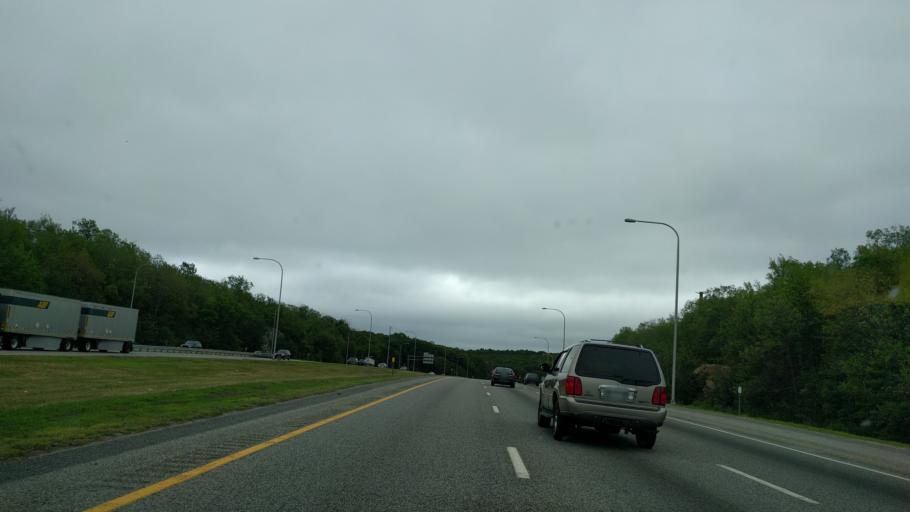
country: US
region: Rhode Island
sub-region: Providence County
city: Johnston
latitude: 41.8169
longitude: -71.5110
